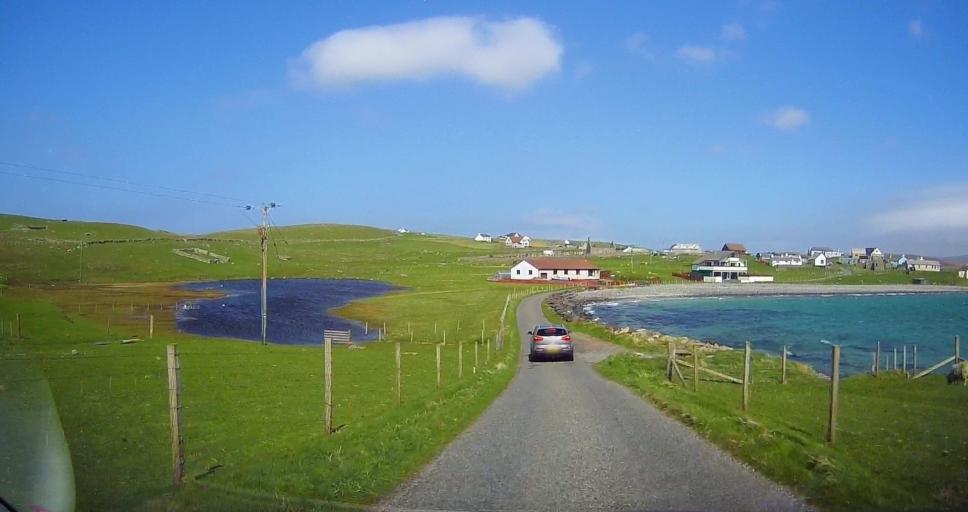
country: GB
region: Scotland
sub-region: Shetland Islands
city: Sandwick
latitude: 60.0629
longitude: -1.3399
